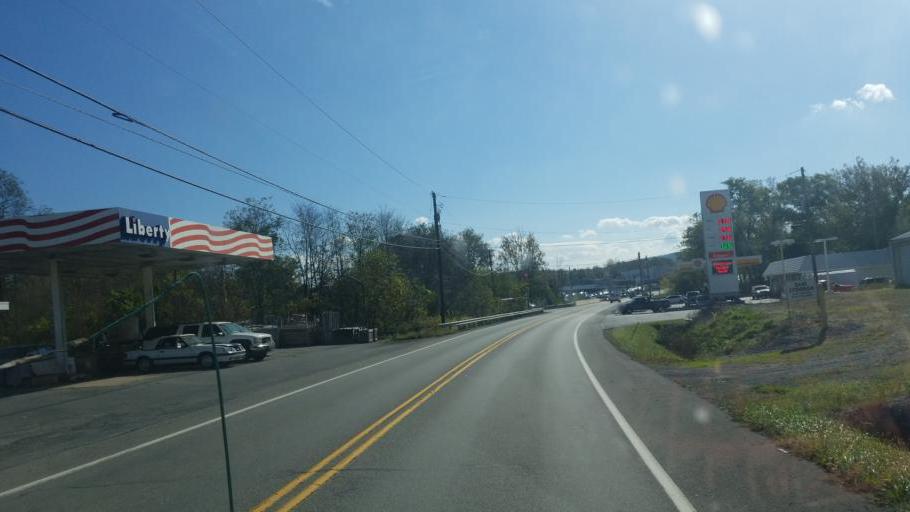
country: US
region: Pennsylvania
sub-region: Bedford County
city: Bedford
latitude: 40.0474
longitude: -78.5310
